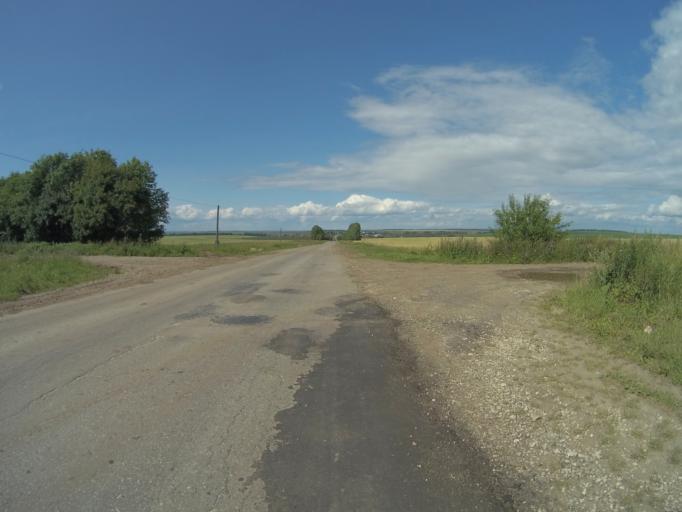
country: RU
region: Vladimir
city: Vladimir
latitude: 56.2435
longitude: 40.3813
